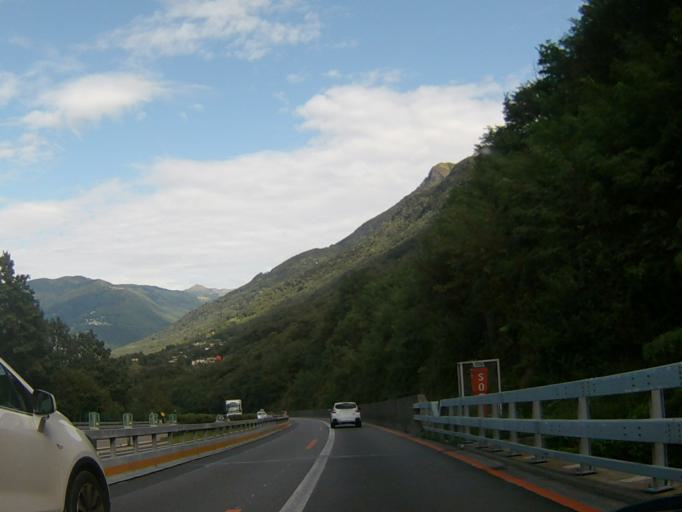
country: CH
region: Ticino
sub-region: Bellinzona District
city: Camorino
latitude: 46.1496
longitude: 8.9754
